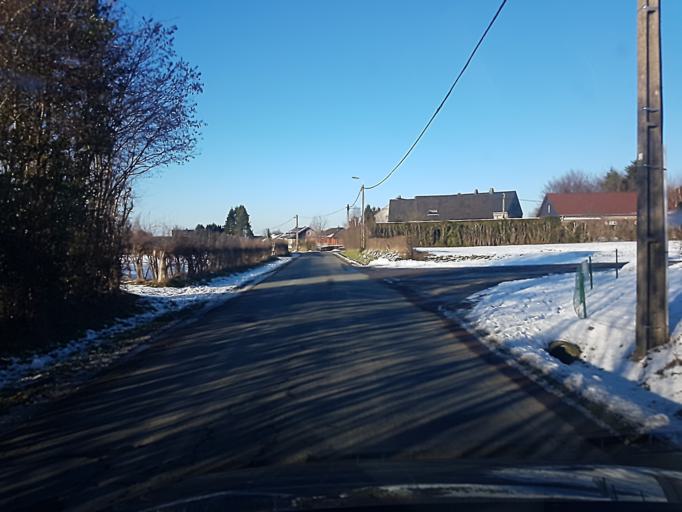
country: BE
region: Wallonia
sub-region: Province de Liege
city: Jalhay
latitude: 50.5550
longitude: 5.9666
